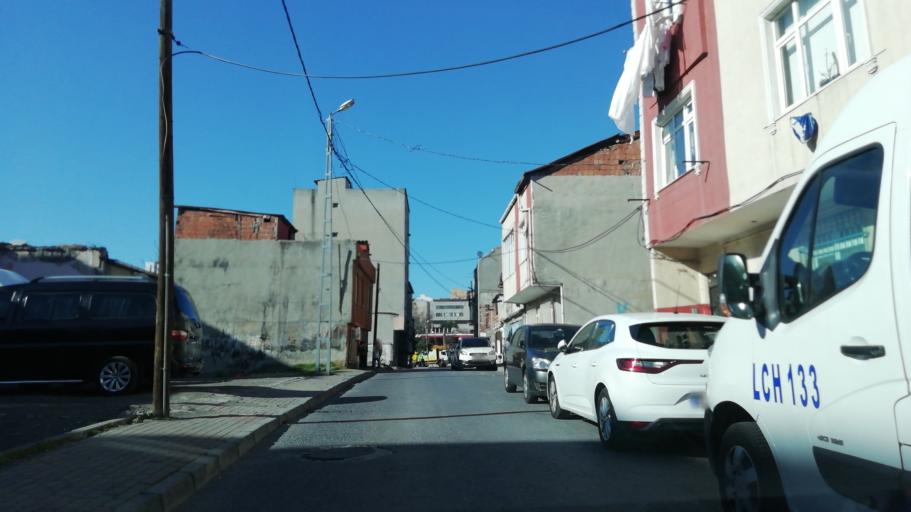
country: TR
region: Istanbul
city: Bagcilar
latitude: 41.0540
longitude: 28.8525
